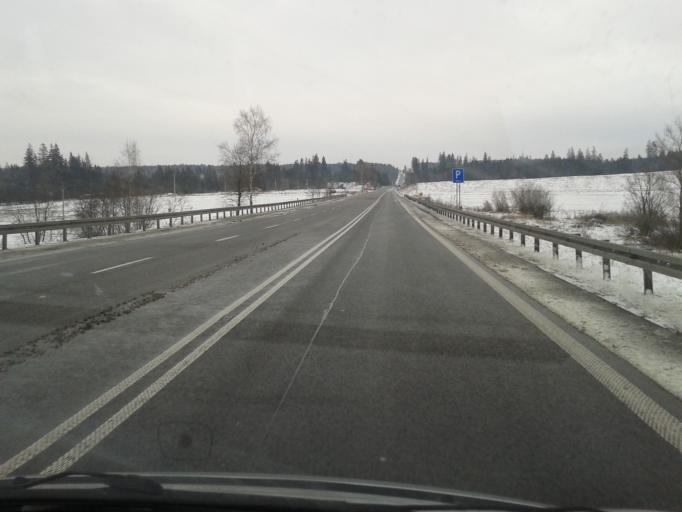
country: PL
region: Lesser Poland Voivodeship
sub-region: Powiat nowotarski
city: Chyzne
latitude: 49.3970
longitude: 19.6477
